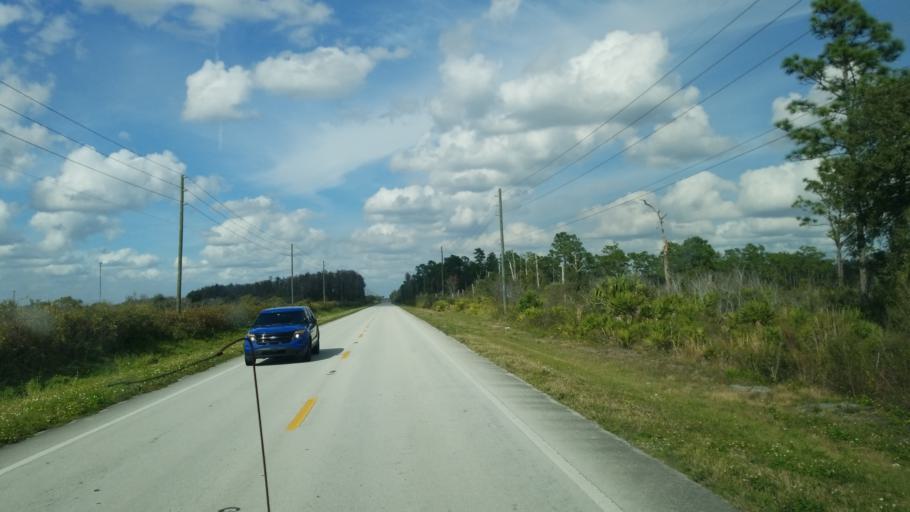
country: US
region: Florida
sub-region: Osceola County
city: Saint Cloud
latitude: 28.1057
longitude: -81.0762
